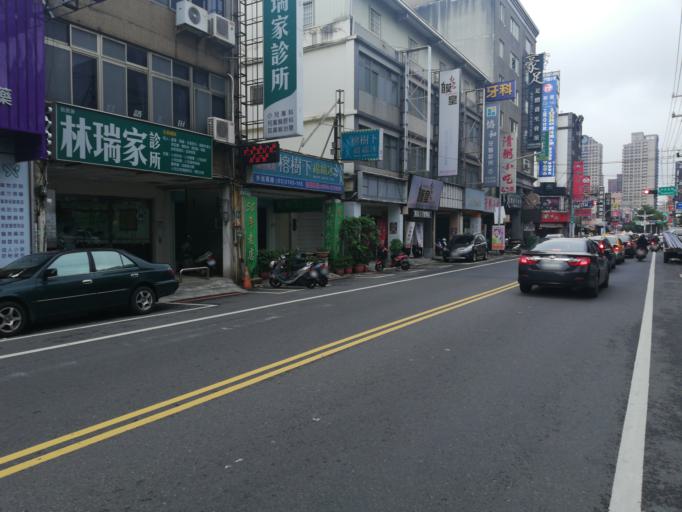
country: TW
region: Taiwan
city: Taoyuan City
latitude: 25.0060
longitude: 121.3039
